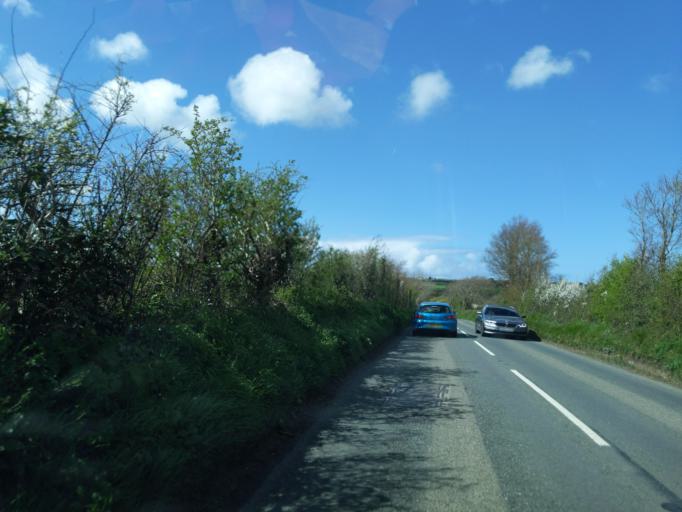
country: GB
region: England
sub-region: Cornwall
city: Wadebridge
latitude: 50.5383
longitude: -4.8537
